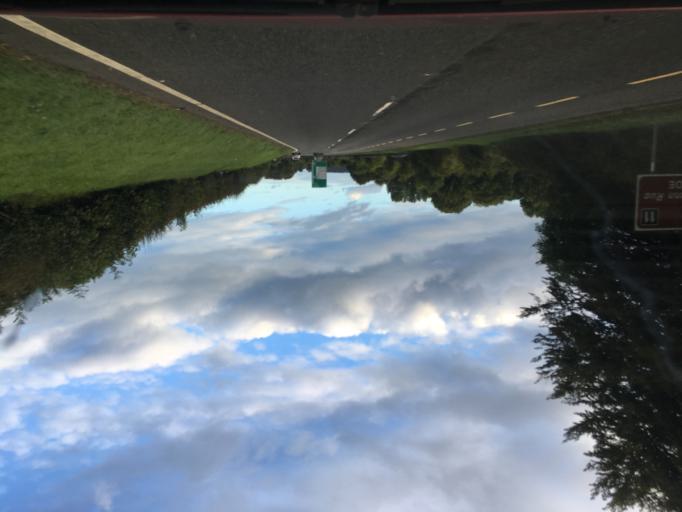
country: IE
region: Leinster
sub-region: Wicklow
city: Kilpedder
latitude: 53.1071
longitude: -6.1069
